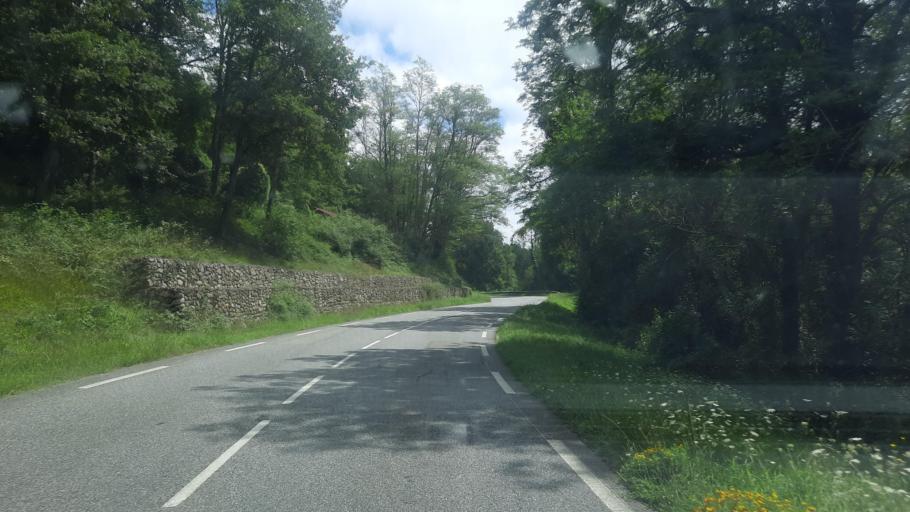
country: FR
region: Midi-Pyrenees
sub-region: Departement des Hautes-Pyrenees
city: Trie-sur-Baise
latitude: 43.2993
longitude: 0.2775
